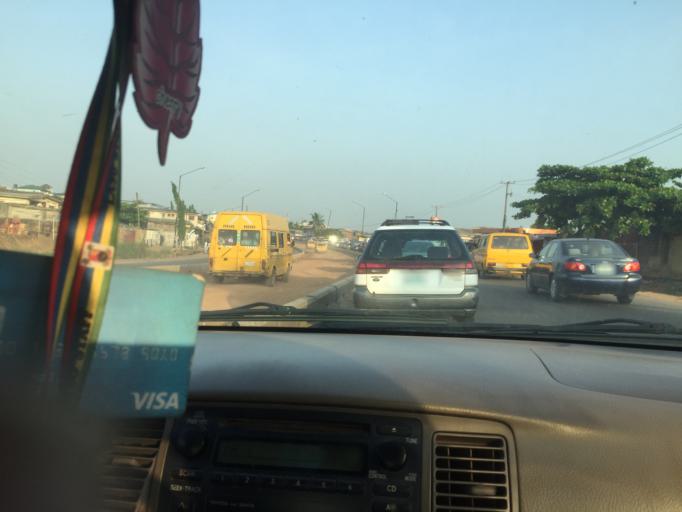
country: NG
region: Lagos
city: Agege
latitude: 6.6053
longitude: 3.3147
